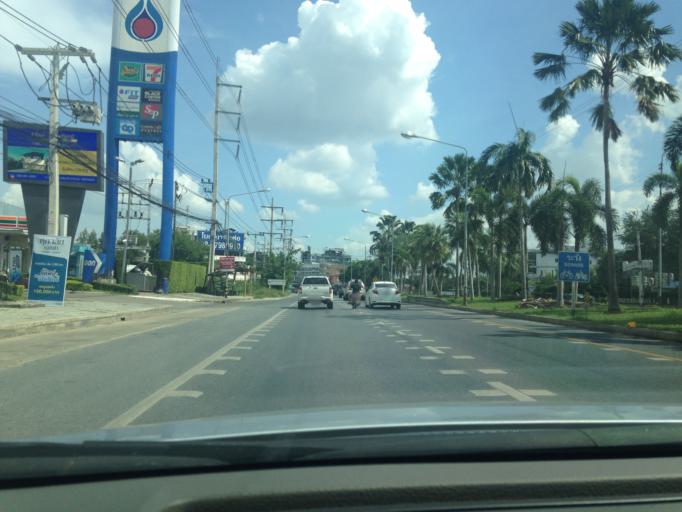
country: TH
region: Phra Nakhon Si Ayutthaya
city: Ban Bang Kadi Pathum Thani
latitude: 13.9862
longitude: 100.5875
